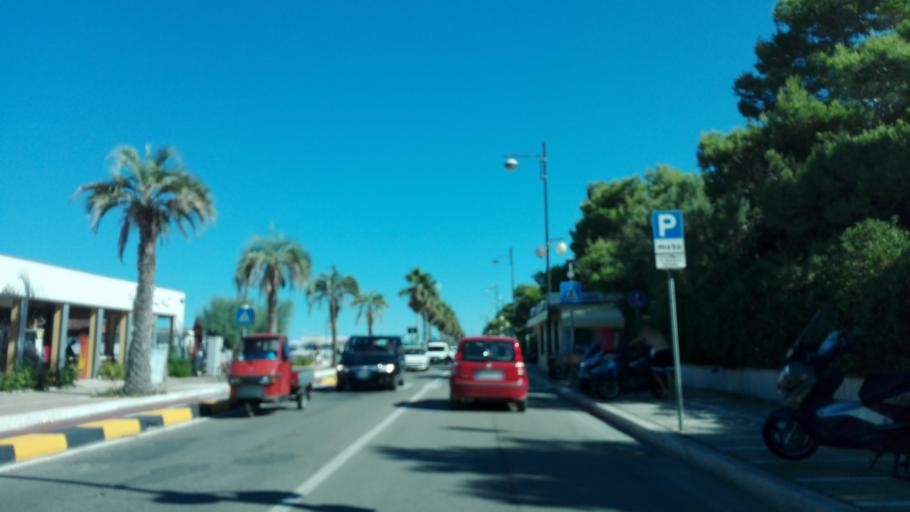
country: IT
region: Abruzzo
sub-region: Provincia di Pescara
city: Montesilvano Marina
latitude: 42.5075
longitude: 14.1714
